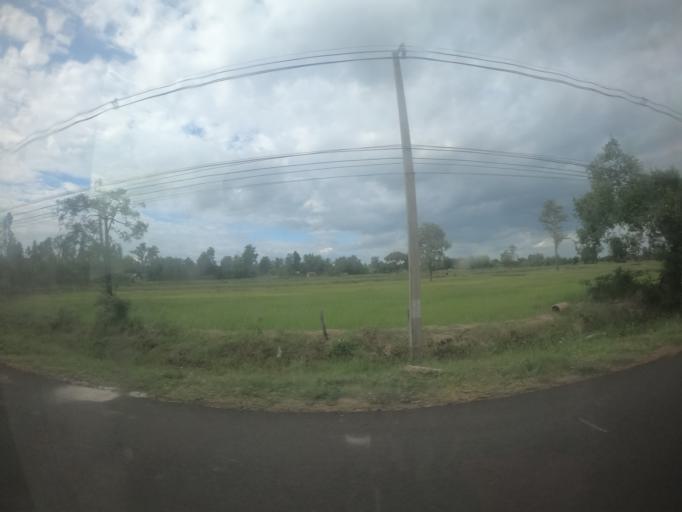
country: TH
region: Surin
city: Prasat
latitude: 14.5606
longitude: 103.4988
